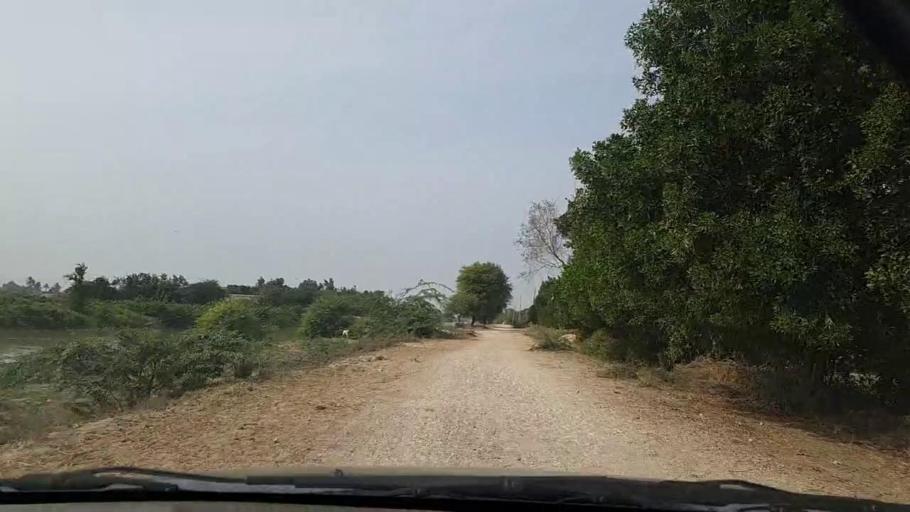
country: PK
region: Sindh
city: Thatta
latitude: 24.5694
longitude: 67.8596
